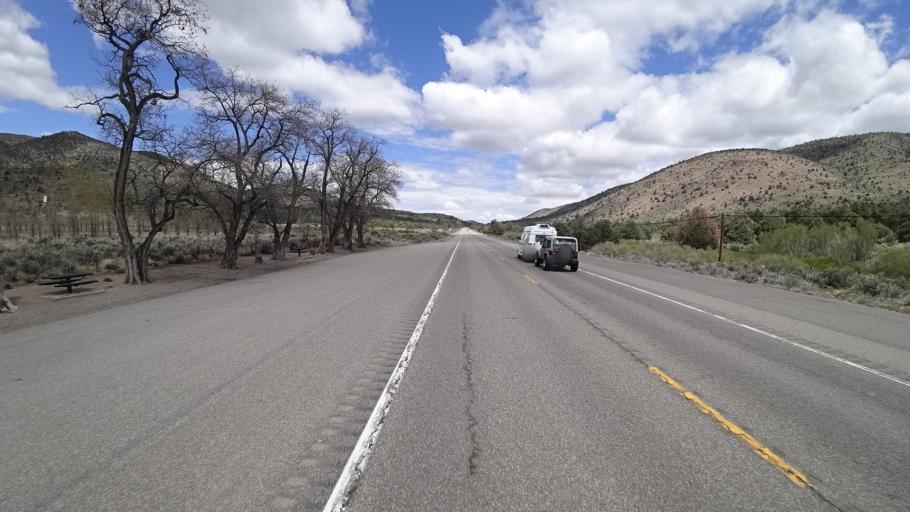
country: US
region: Nevada
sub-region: Douglas County
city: Gardnerville Ranchos
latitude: 38.7483
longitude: -119.5679
